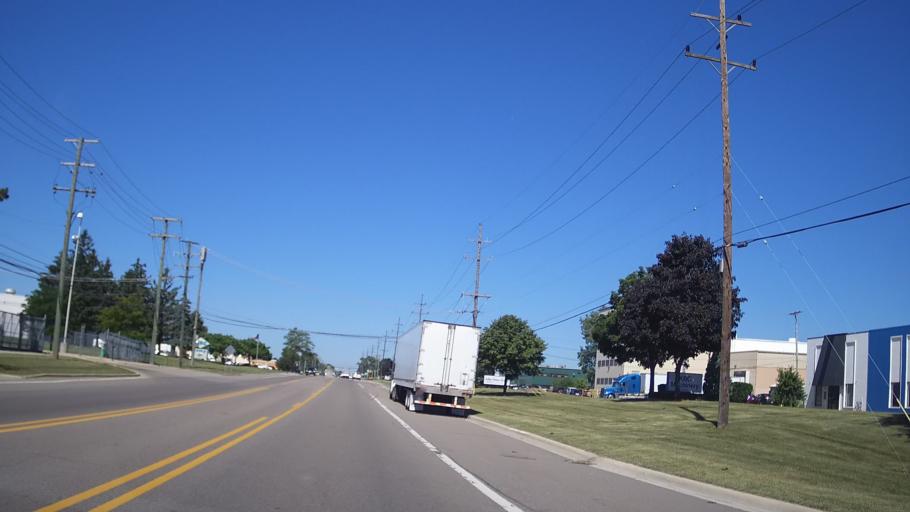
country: US
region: Michigan
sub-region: Macomb County
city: Sterling Heights
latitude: 42.5945
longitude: -83.0446
